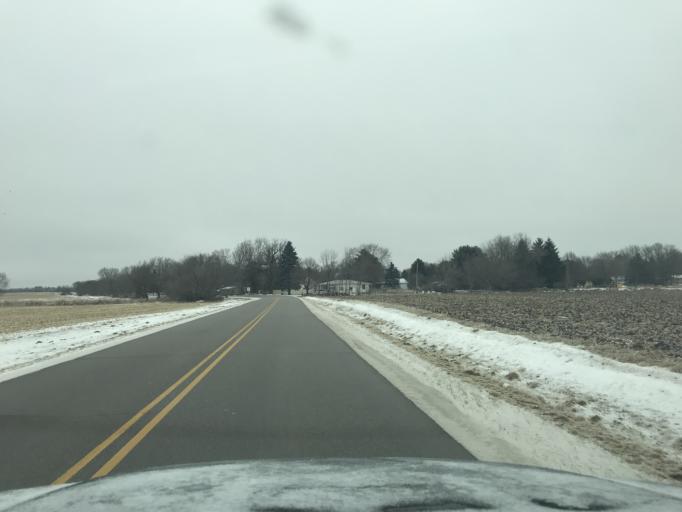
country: US
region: Wisconsin
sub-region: Dane County
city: Cottage Grove
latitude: 43.0916
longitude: -89.2353
